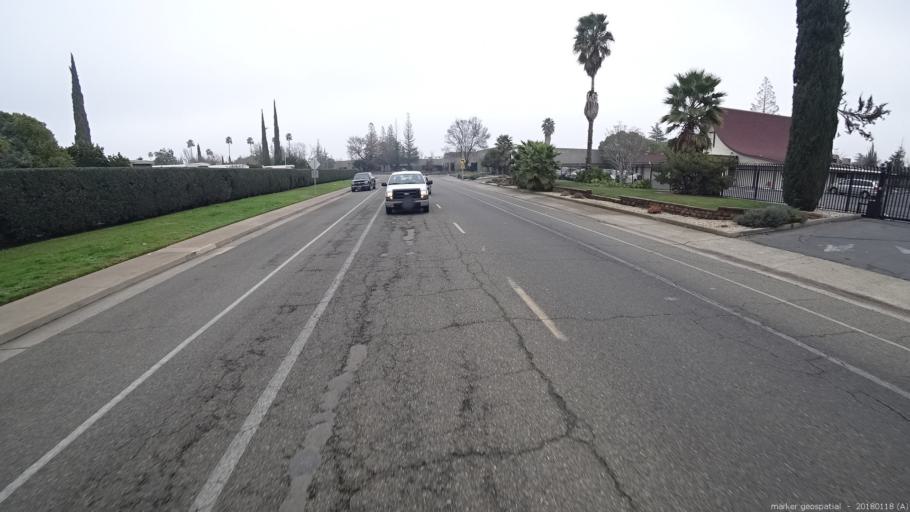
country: US
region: California
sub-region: Sacramento County
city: Rancho Cordova
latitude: 38.5767
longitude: -121.3153
